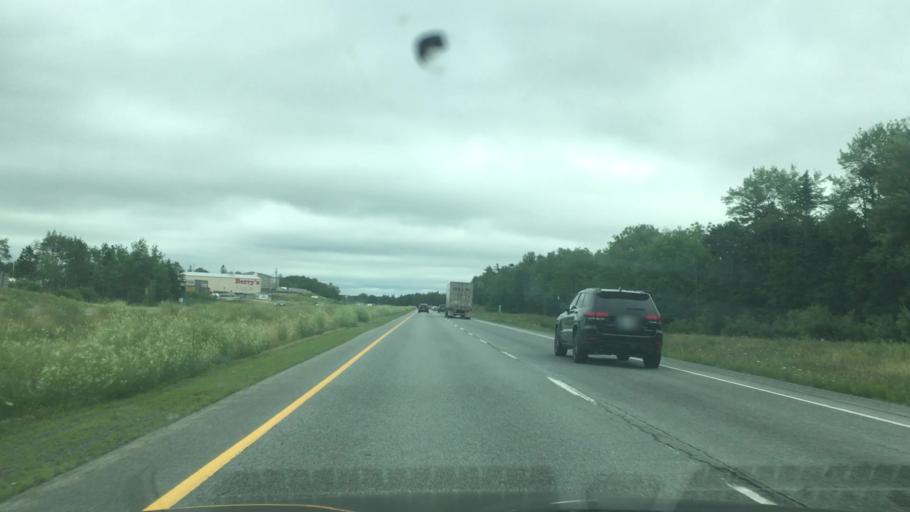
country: CA
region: Nova Scotia
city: Cole Harbour
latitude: 44.9674
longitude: -63.5206
